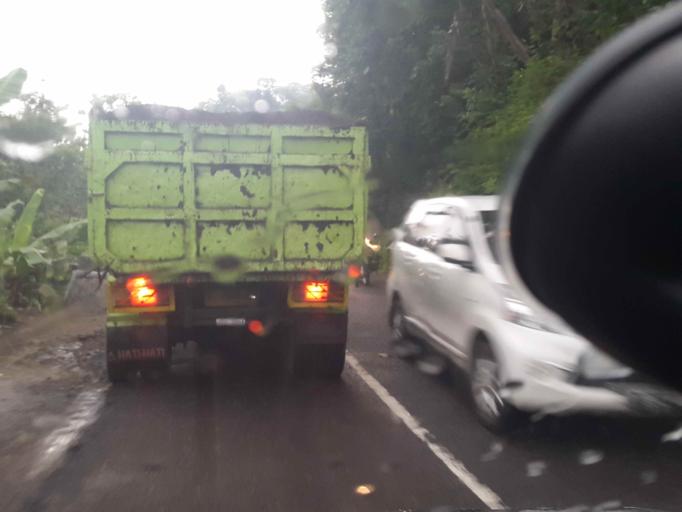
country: ID
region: Central Java
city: Garbi
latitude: -7.4997
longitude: 109.2161
